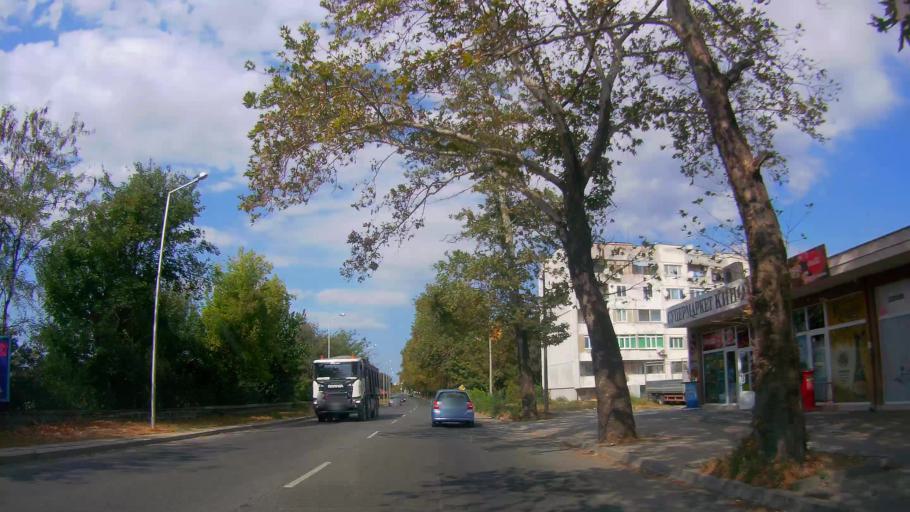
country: BG
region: Burgas
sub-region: Obshtina Aytos
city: Aytos
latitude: 42.6969
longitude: 27.2601
